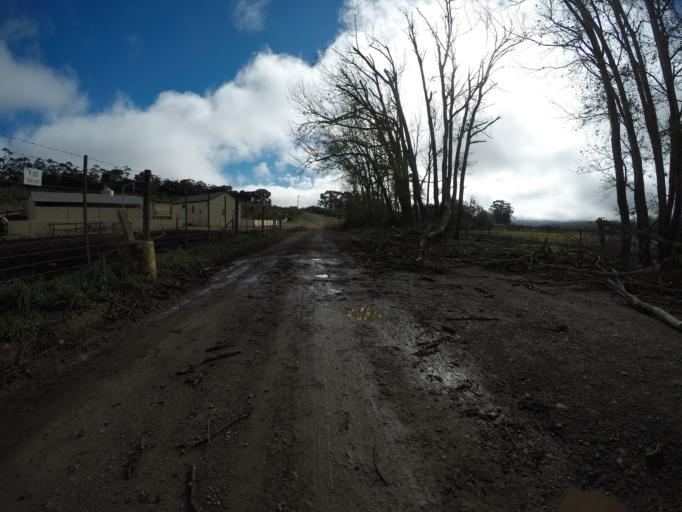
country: ZA
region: Western Cape
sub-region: Cape Winelands District Municipality
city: Ashton
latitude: -34.1245
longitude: 19.8104
